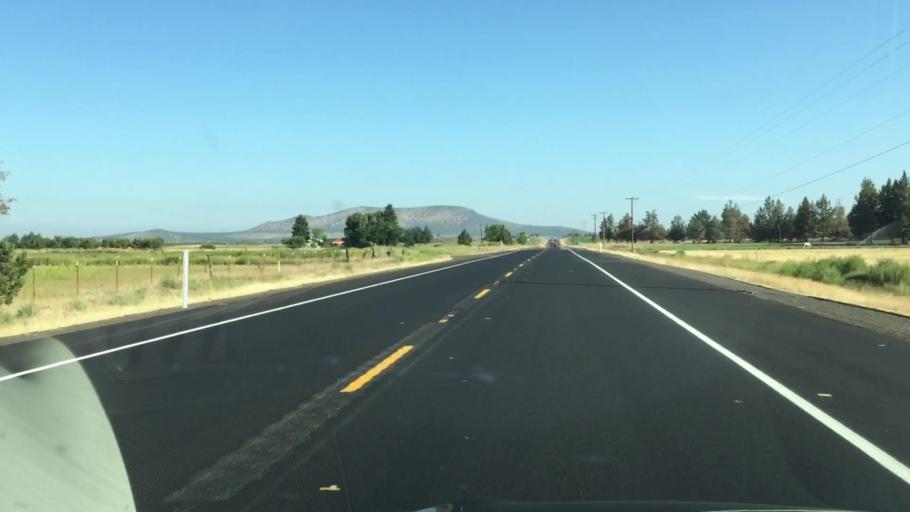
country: US
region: Oregon
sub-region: Deschutes County
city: Terrebonne
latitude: 44.4132
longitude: -121.1991
